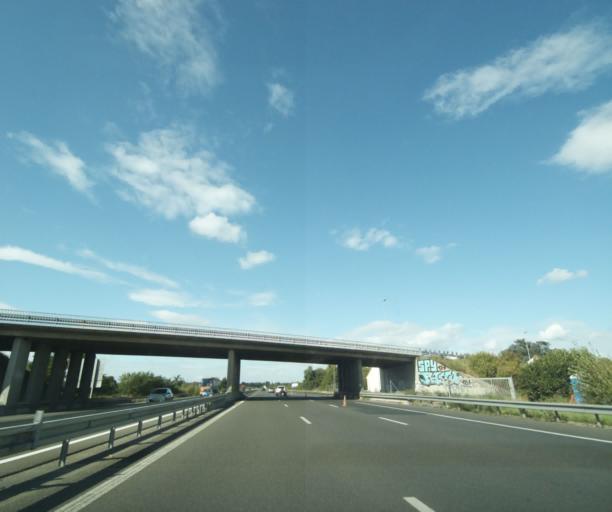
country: FR
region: Centre
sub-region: Departement du Loiret
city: Saint-Pryve-Saint-Mesmin
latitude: 47.8791
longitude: 1.8619
